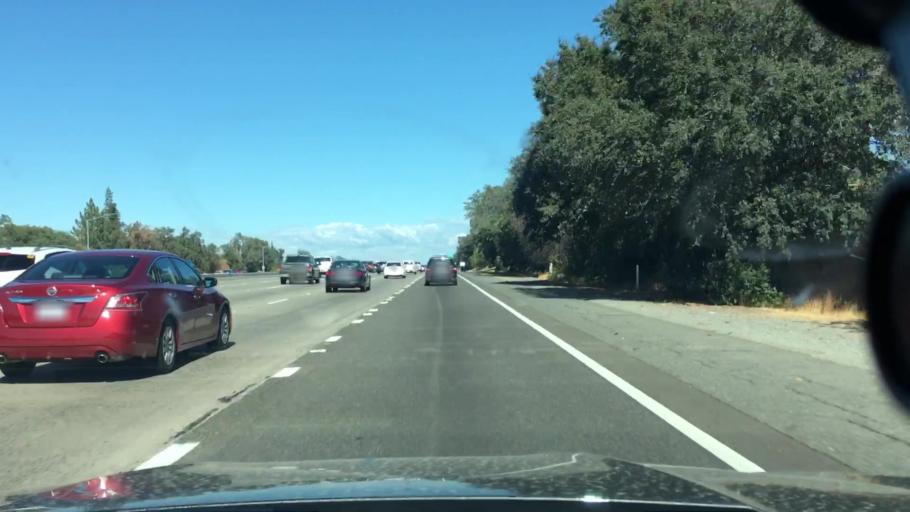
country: US
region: California
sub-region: Sacramento County
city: Foothill Farms
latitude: 38.6773
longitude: -121.3420
